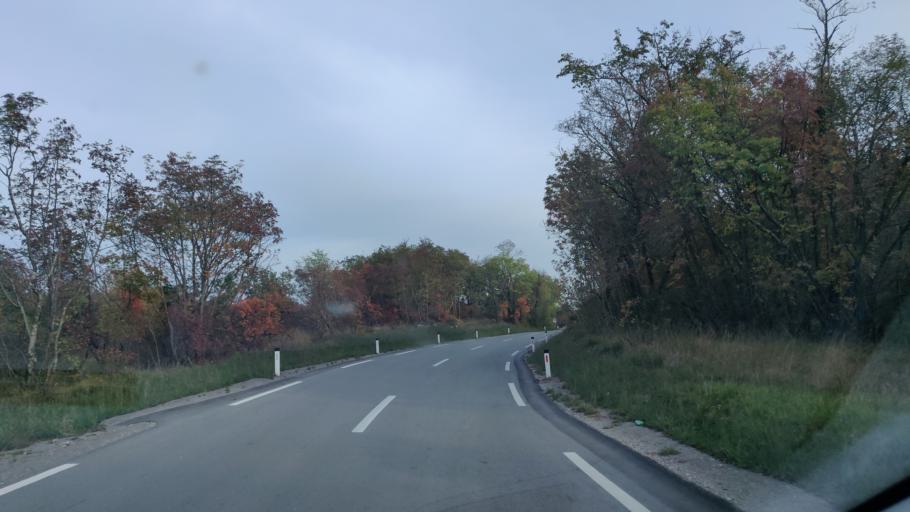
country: SI
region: Miren-Kostanjevica
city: Bilje
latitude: 45.8472
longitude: 13.6235
